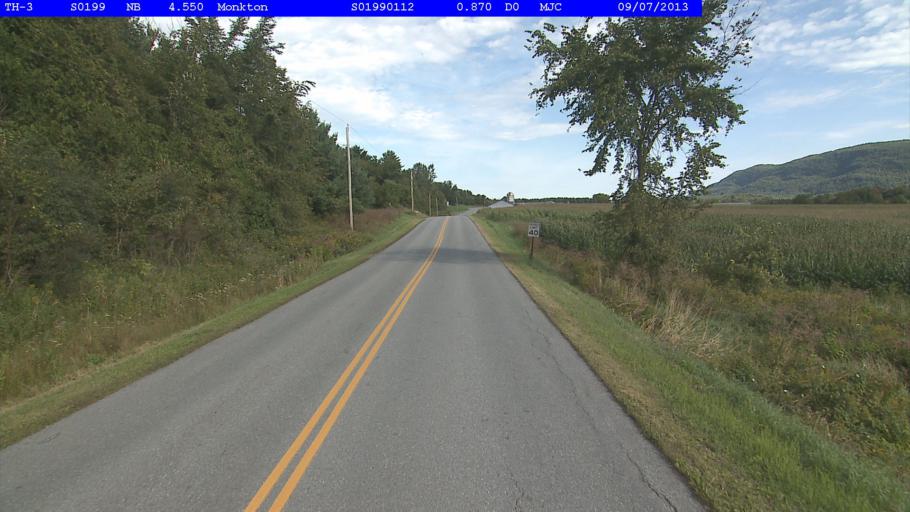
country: US
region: Vermont
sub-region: Addison County
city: Bristol
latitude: 44.1931
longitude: -73.1091
